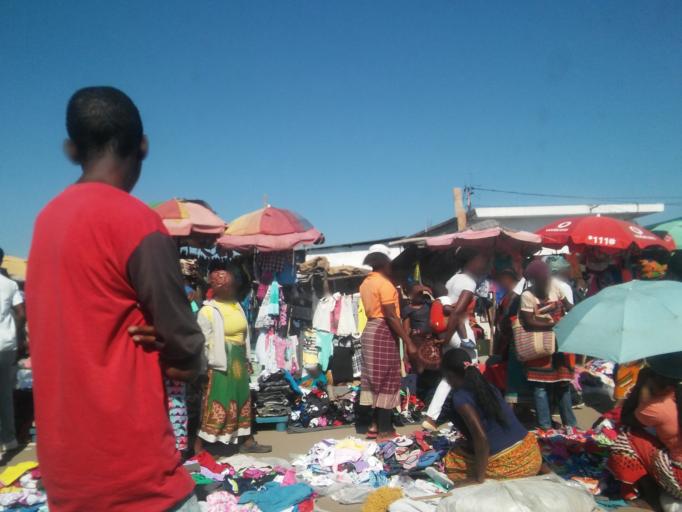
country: MZ
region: Maputo City
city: Maputo
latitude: -25.8308
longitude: 32.5731
